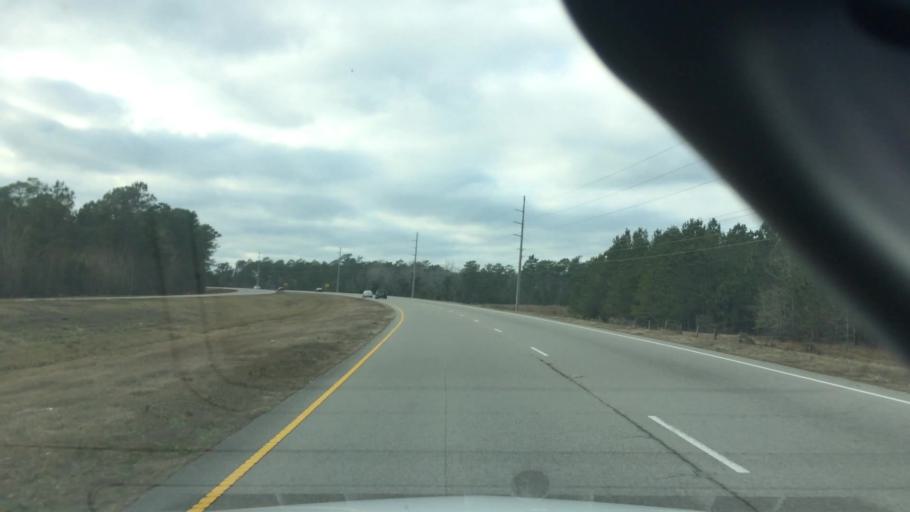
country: US
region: North Carolina
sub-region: Brunswick County
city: Shallotte
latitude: 33.9894
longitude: -78.3829
